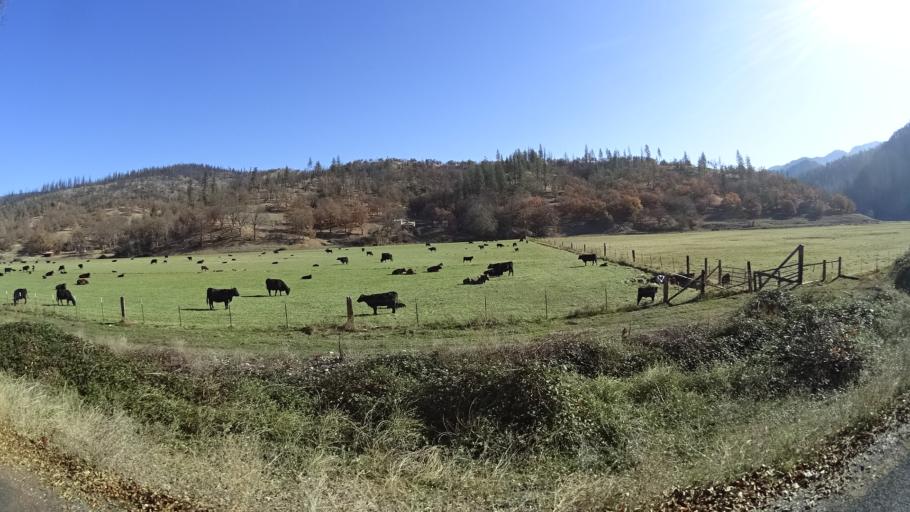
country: US
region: California
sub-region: Siskiyou County
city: Happy Camp
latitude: 41.8287
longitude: -123.0064
